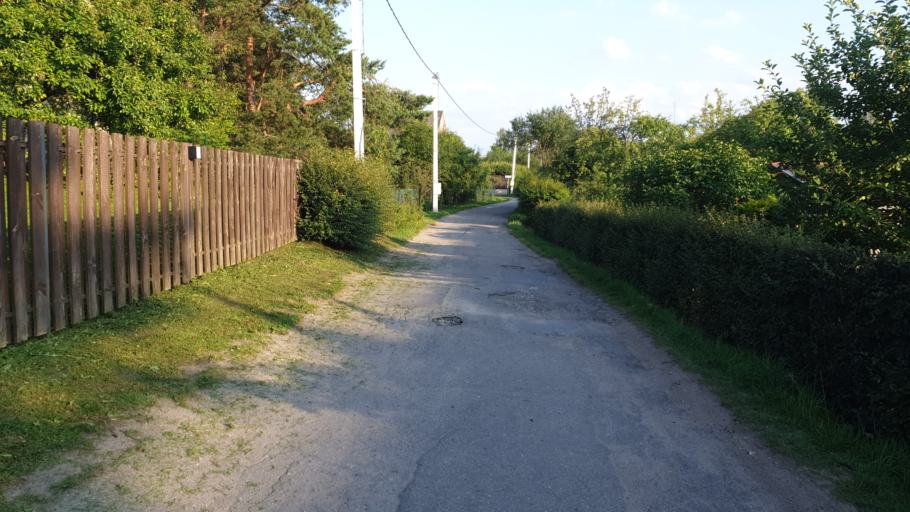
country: LT
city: Grigiskes
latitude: 54.7650
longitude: 25.0292
